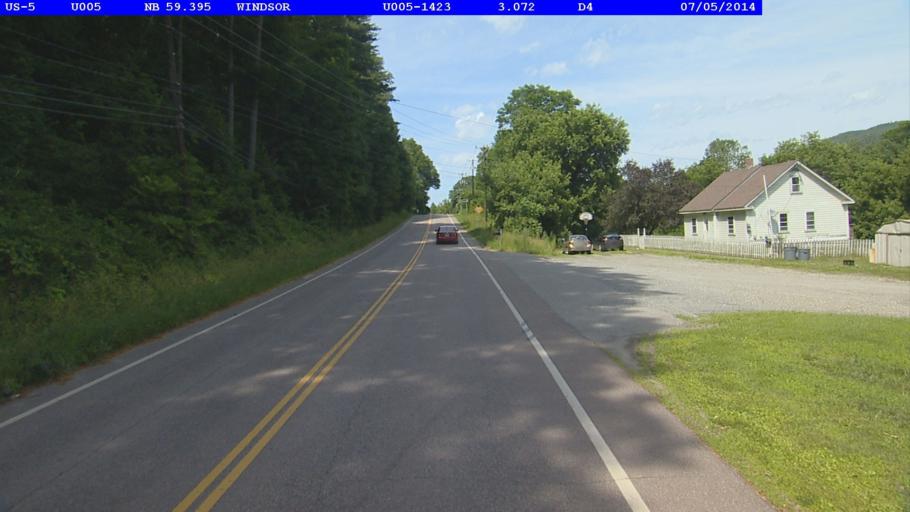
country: US
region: Vermont
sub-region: Windsor County
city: Windsor
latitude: 43.4716
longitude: -72.3902
